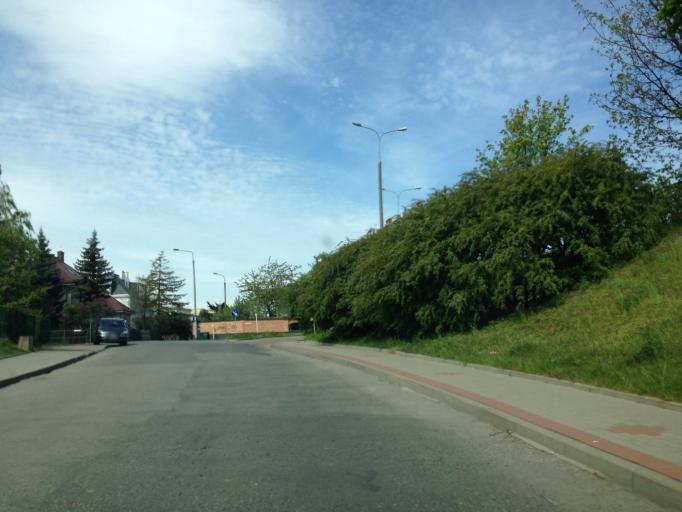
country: PL
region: Pomeranian Voivodeship
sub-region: Gdynia
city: Gdynia
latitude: 54.5120
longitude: 18.5465
